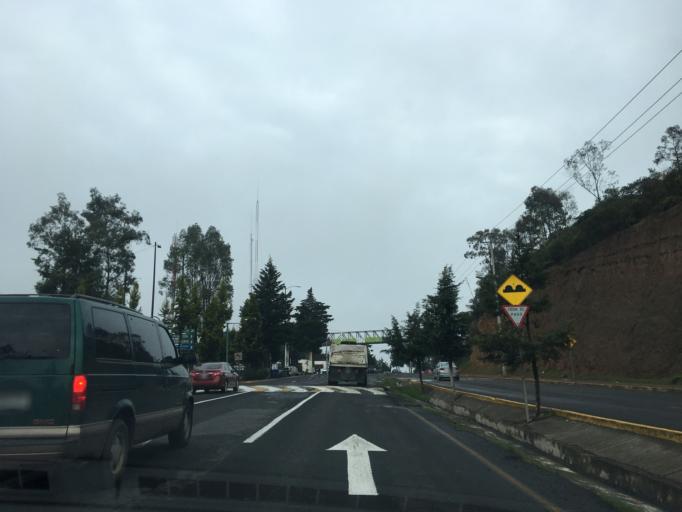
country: MX
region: Mexico
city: Ciudad Lopez Mateos
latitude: 19.5546
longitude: -99.2949
